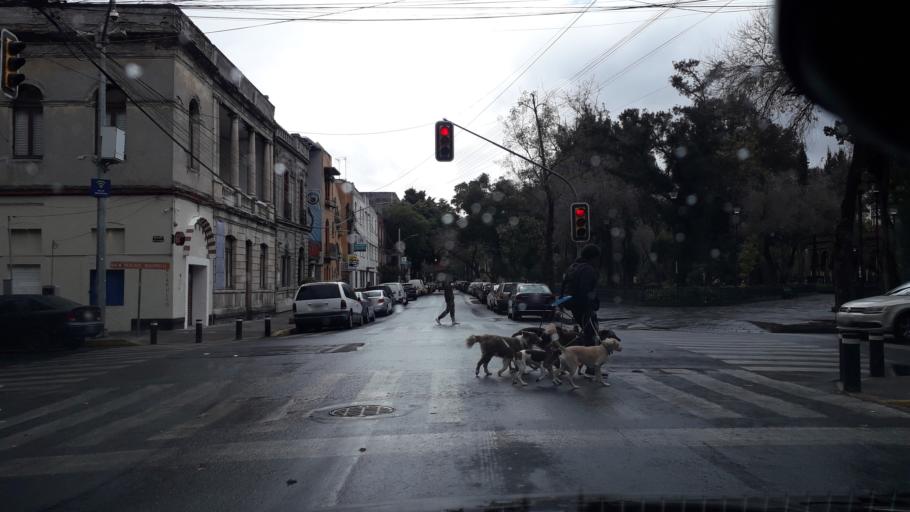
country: MX
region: Mexico City
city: Cuauhtemoc
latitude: 19.4506
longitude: -99.1560
